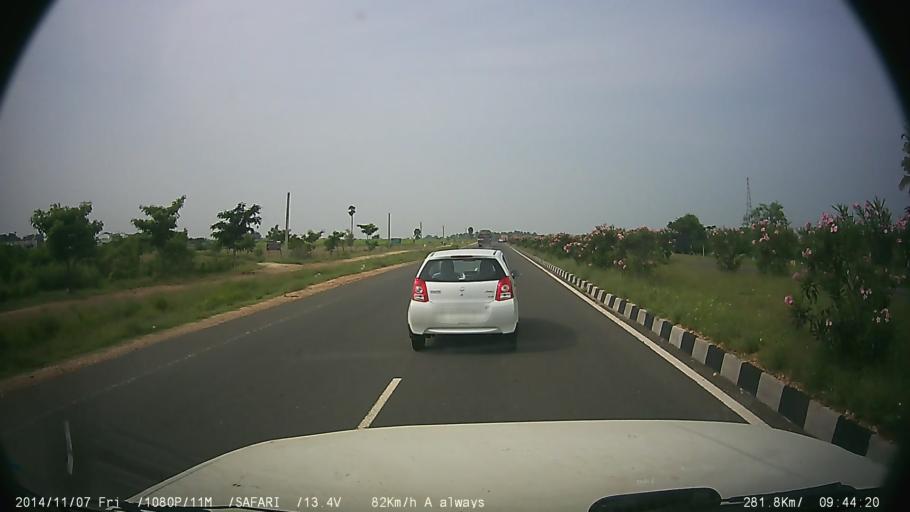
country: IN
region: Tamil Nadu
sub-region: Erode
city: Perundurai
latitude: 11.2949
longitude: 77.5930
